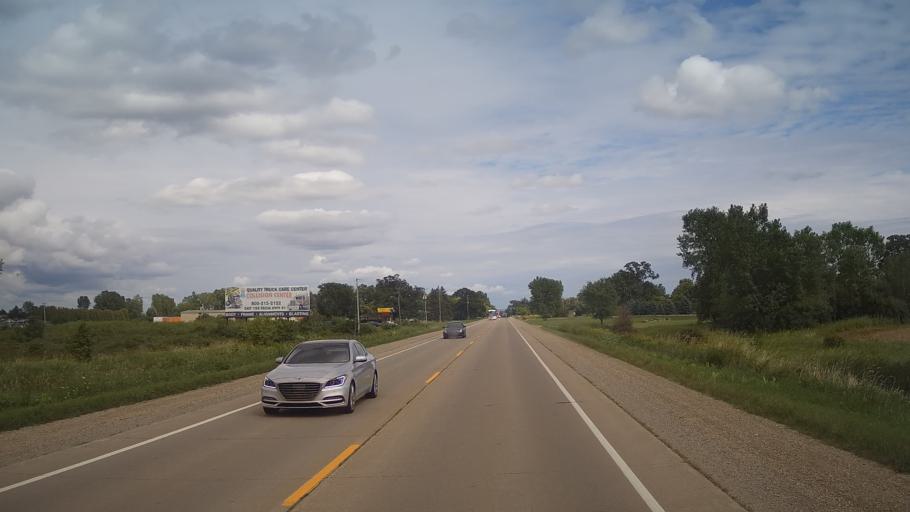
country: US
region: Wisconsin
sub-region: Winnebago County
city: Oshkosh
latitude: 44.0331
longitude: -88.6417
